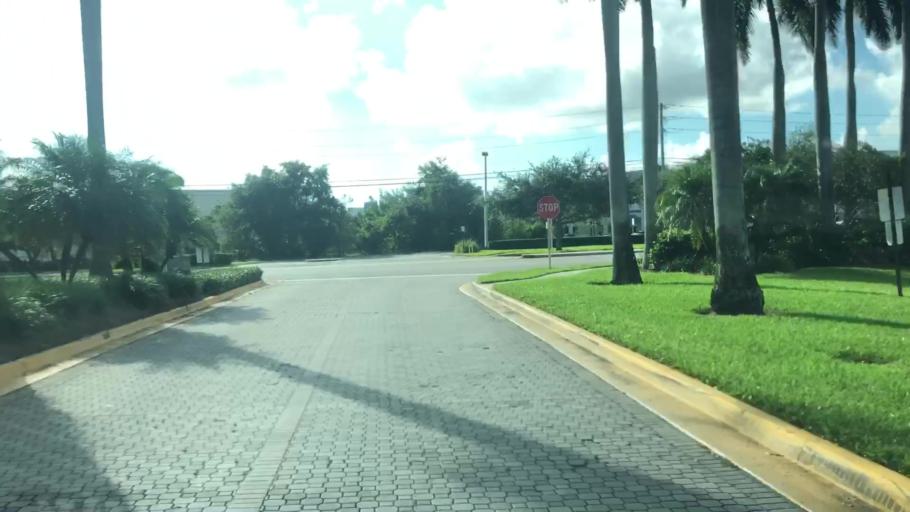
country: US
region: Florida
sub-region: Broward County
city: Kendall Green
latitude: 26.2637
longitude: -80.1405
